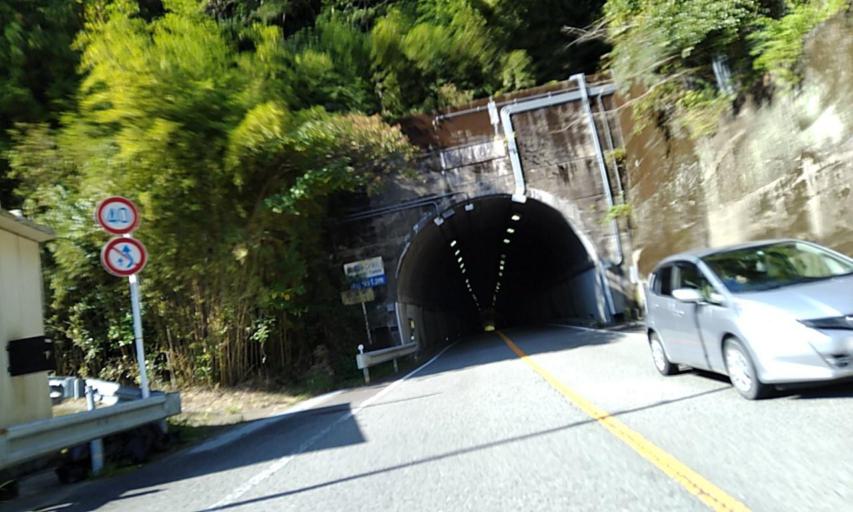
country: JP
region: Wakayama
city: Gobo
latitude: 33.9900
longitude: 135.1779
